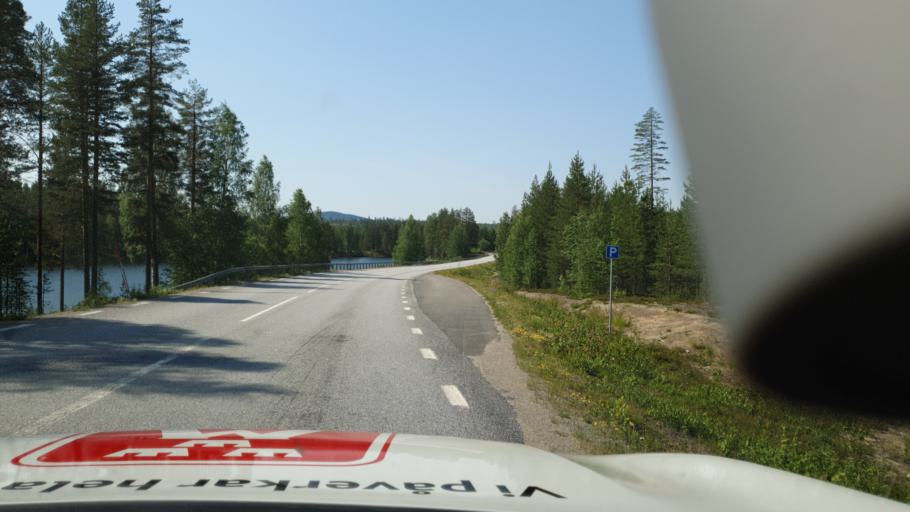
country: SE
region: Vaesterbotten
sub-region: Norsjo Kommun
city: Norsjoe
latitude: 64.9678
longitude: 19.7132
